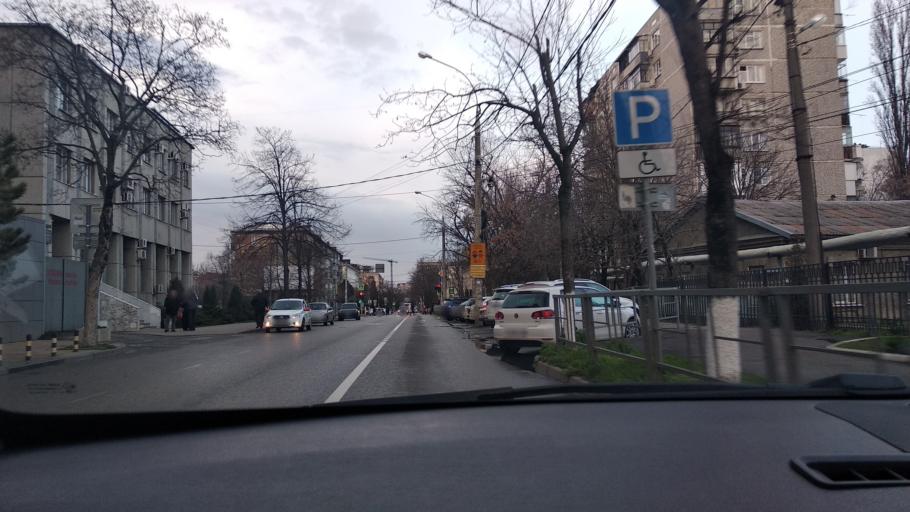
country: RU
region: Krasnodarskiy
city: Krasnodar
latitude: 45.0458
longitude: 38.9753
